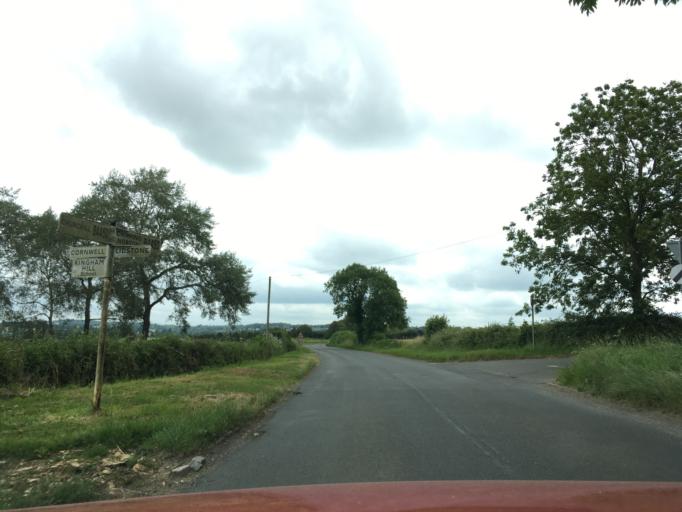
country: GB
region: England
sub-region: Oxfordshire
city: Chipping Norton
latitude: 51.9282
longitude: -1.5757
